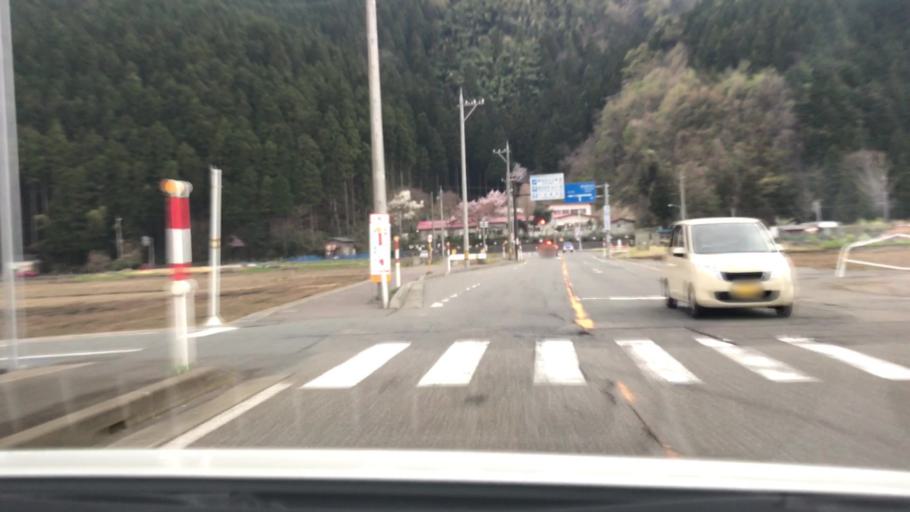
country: JP
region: Fukui
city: Fukui-shi
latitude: 36.0884
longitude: 136.1818
